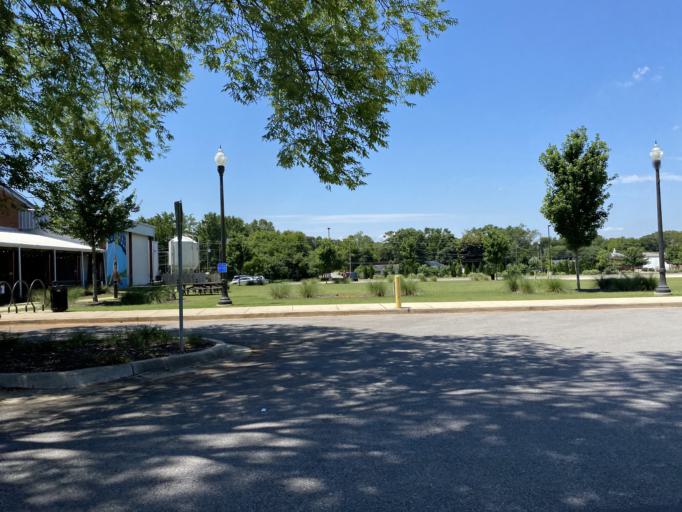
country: US
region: Alabama
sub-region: Madison County
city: Huntsville
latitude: 34.7209
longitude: -86.6064
